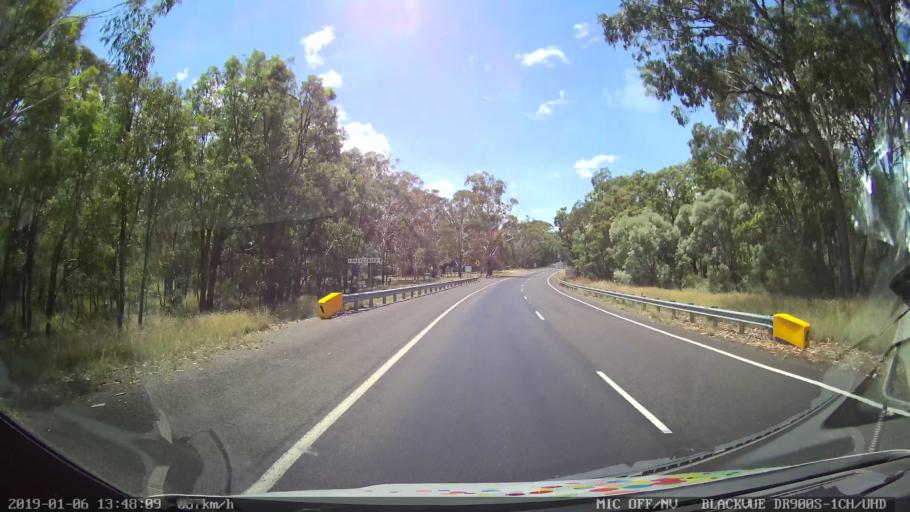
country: AU
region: New South Wales
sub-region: Tamworth Municipality
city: Kootingal
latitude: -30.9555
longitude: 151.1065
